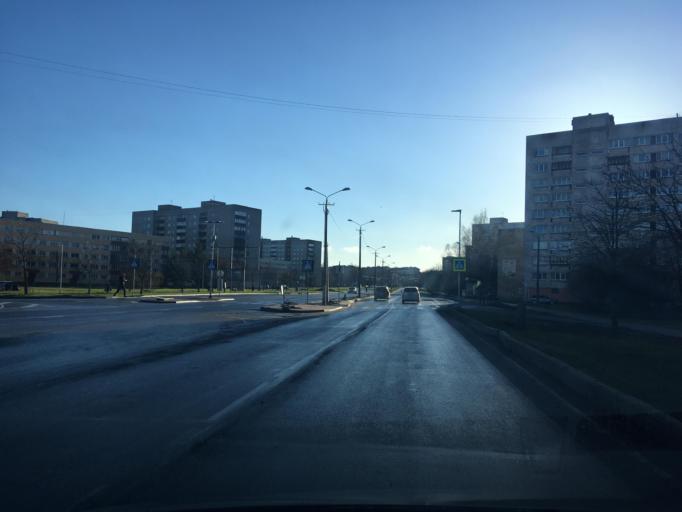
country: EE
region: Ida-Virumaa
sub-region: Narva linn
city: Narva
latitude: 59.3859
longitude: 28.1763
